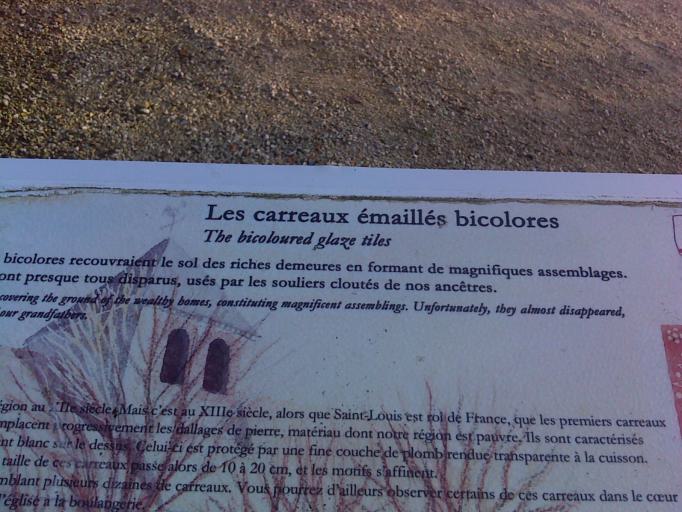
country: FR
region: Champagne-Ardenne
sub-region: Departement de l'Aube
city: Lusigny-sur-Barse
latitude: 48.2494
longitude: 4.3326
